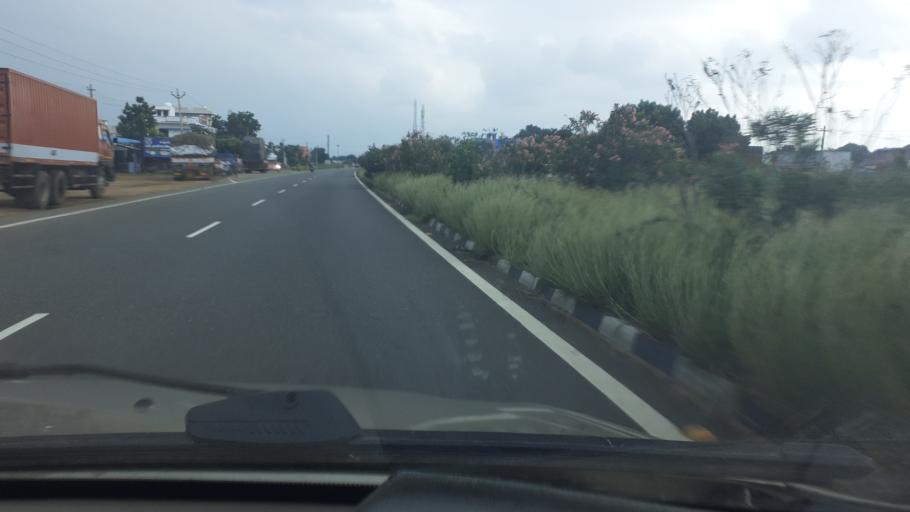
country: IN
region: Tamil Nadu
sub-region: Madurai
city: Kallupatti
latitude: 9.7025
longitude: 77.9730
